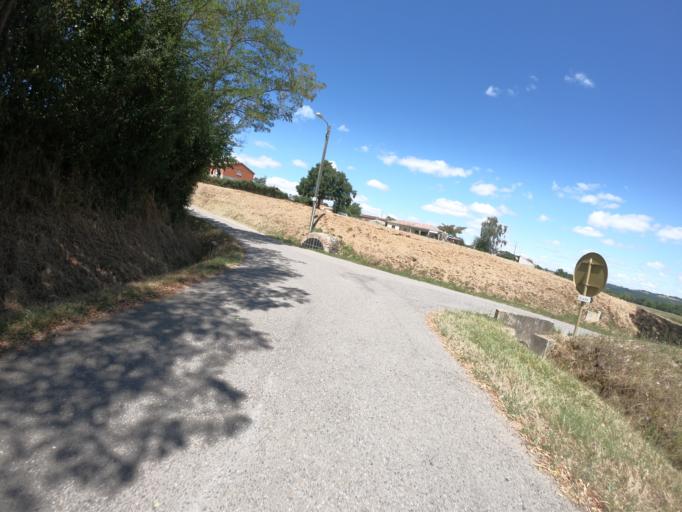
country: FR
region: Midi-Pyrenees
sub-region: Departement de l'Ariege
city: La Tour-du-Crieu
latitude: 43.0876
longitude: 1.7212
